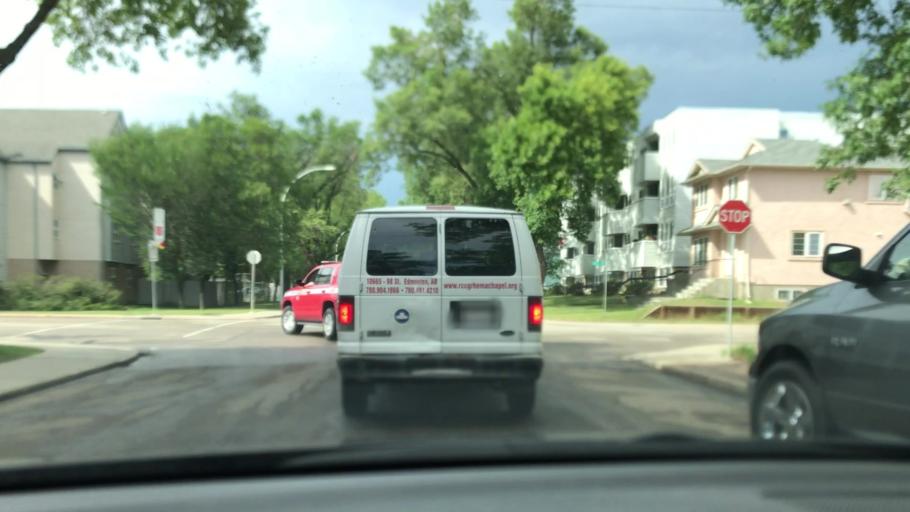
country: CA
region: Alberta
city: Edmonton
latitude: 53.5482
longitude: -113.4767
